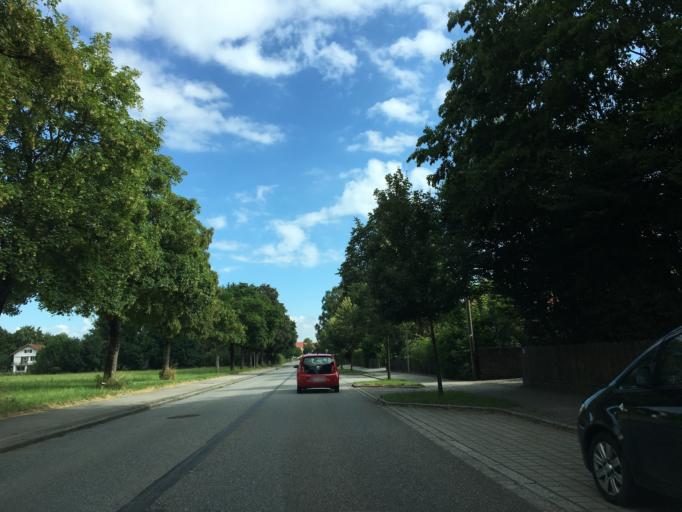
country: DE
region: Bavaria
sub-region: Upper Bavaria
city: Sauerlach
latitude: 47.9675
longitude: 11.6536
